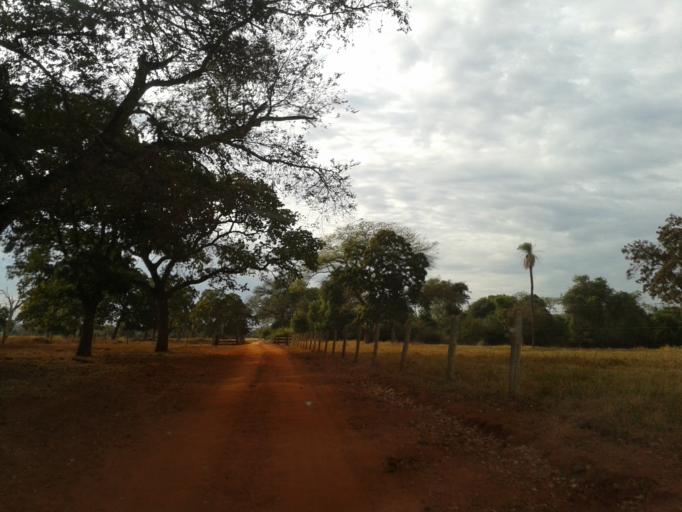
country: BR
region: Minas Gerais
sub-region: Santa Vitoria
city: Santa Vitoria
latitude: -18.7506
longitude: -50.2042
